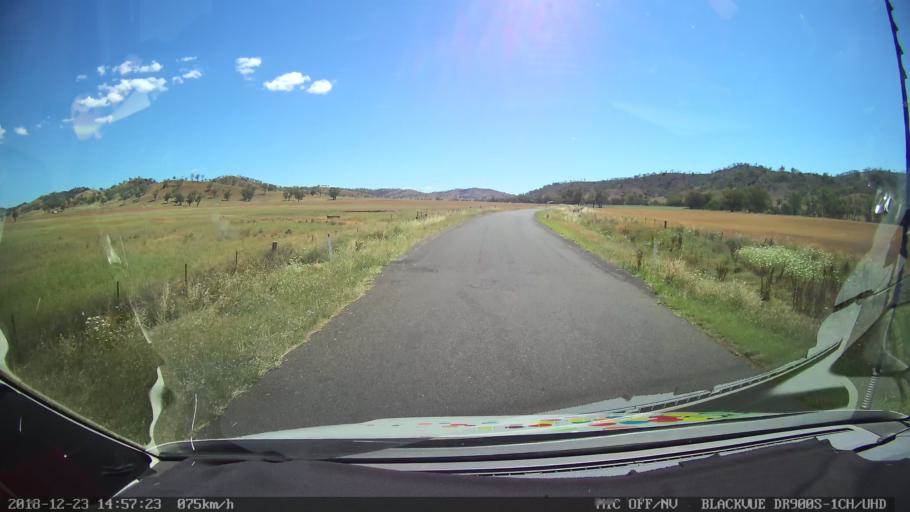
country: AU
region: New South Wales
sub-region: Tamworth Municipality
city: Manilla
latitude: -30.7094
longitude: 150.8250
